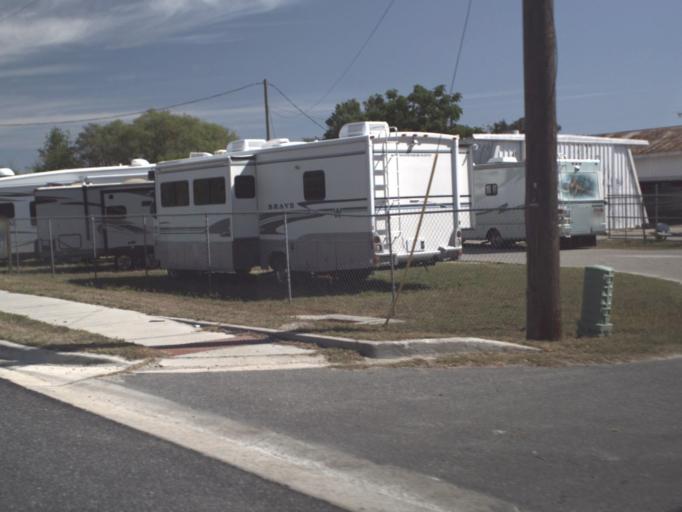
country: US
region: Florida
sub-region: Lake County
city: Fruitland Park
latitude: 28.8772
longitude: -81.9063
